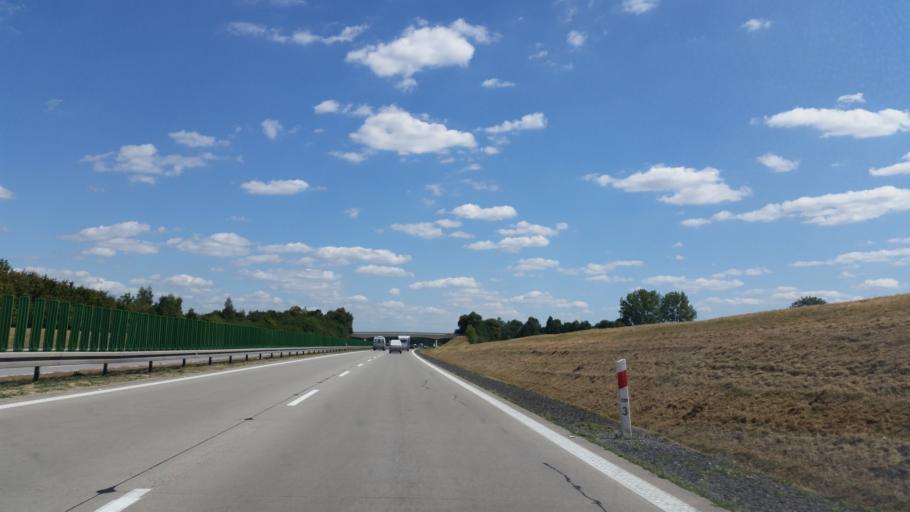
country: PL
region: Lower Silesian Voivodeship
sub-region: Powiat wroclawski
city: Katy Wroclawskie
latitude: 51.0290
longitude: 16.6550
